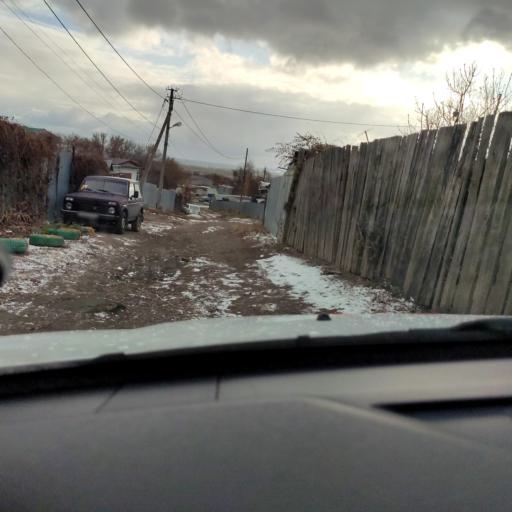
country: RU
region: Samara
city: Samara
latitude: 53.1783
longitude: 50.1545
